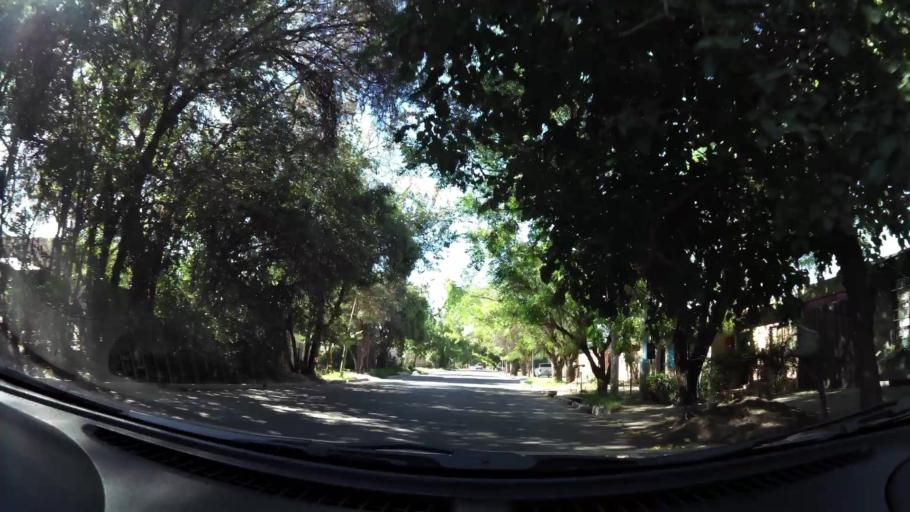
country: AR
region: Mendoza
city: Las Heras
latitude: -32.8346
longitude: -68.8293
